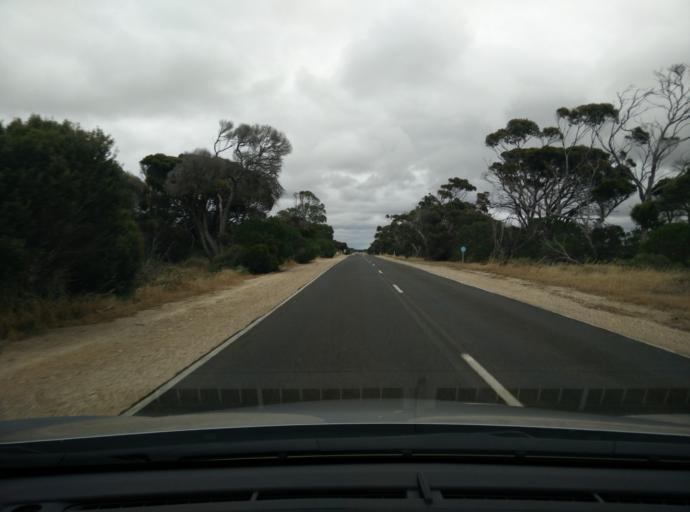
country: AU
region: South Australia
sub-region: Kangaroo Island
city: Kingscote
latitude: -35.6766
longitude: 137.5810
